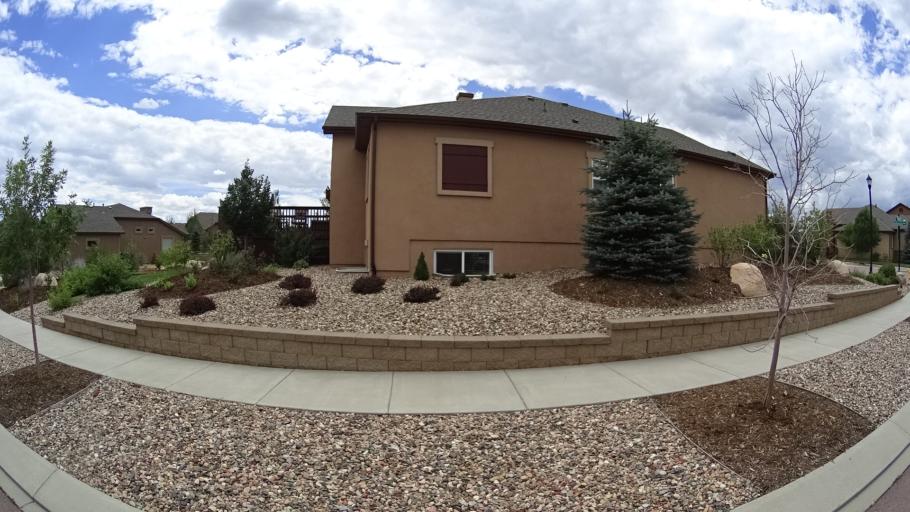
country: US
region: Colorado
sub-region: El Paso County
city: Gleneagle
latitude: 39.0230
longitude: -104.8011
